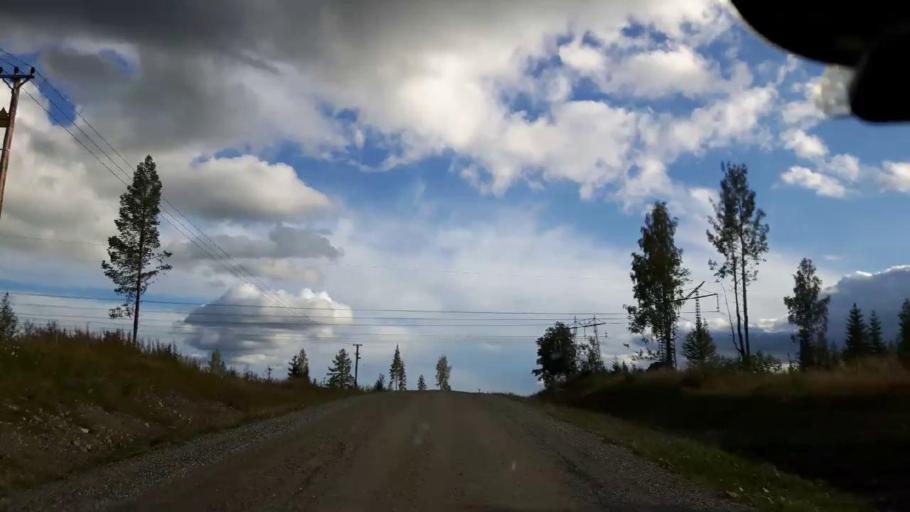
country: SE
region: Jaemtland
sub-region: Stroemsunds Kommun
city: Stroemsund
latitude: 63.3102
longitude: 15.5948
